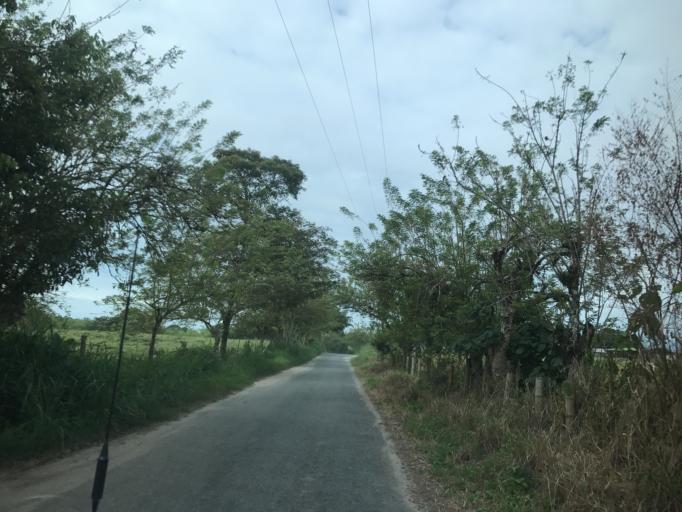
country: CO
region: Quindio
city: Montenegro
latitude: 4.5456
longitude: -75.8279
